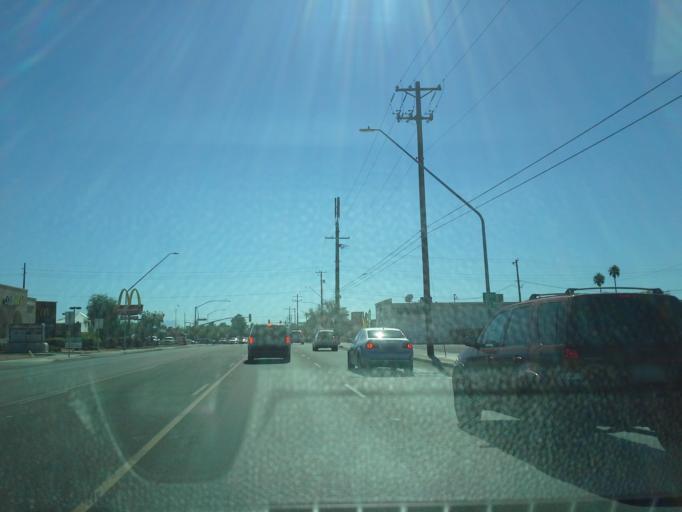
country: US
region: Arizona
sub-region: Pima County
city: Catalina Foothills
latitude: 32.2666
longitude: -110.9438
